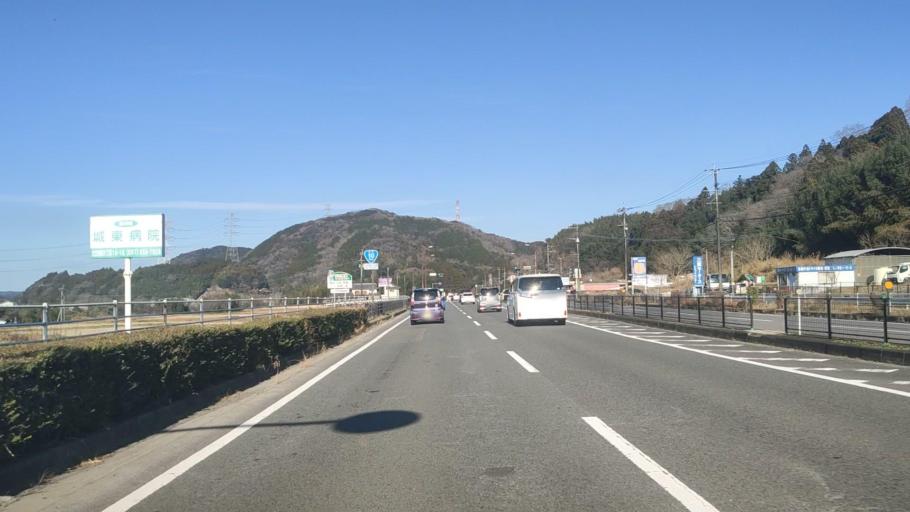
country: JP
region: Oita
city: Oita
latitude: 33.1037
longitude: 131.6530
